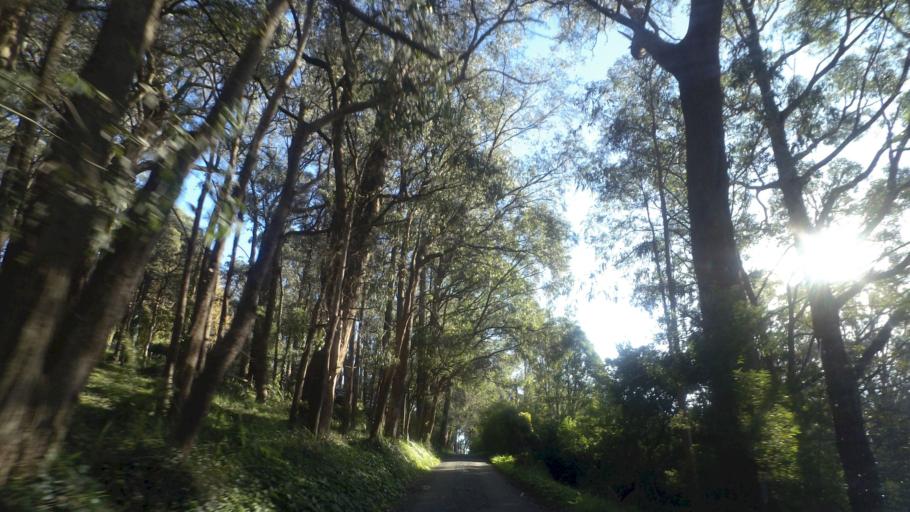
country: AU
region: Victoria
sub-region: Yarra Ranges
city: Kalorama
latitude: -37.8138
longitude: 145.3754
